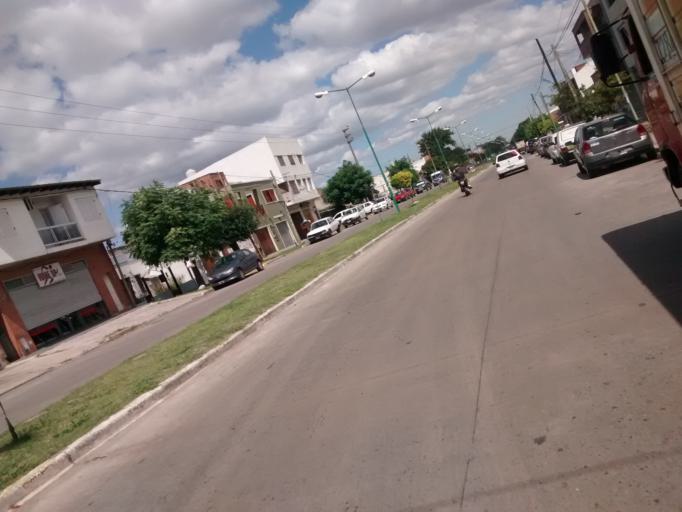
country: AR
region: Buenos Aires
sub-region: Partido de La Plata
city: La Plata
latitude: -34.9554
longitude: -57.9648
